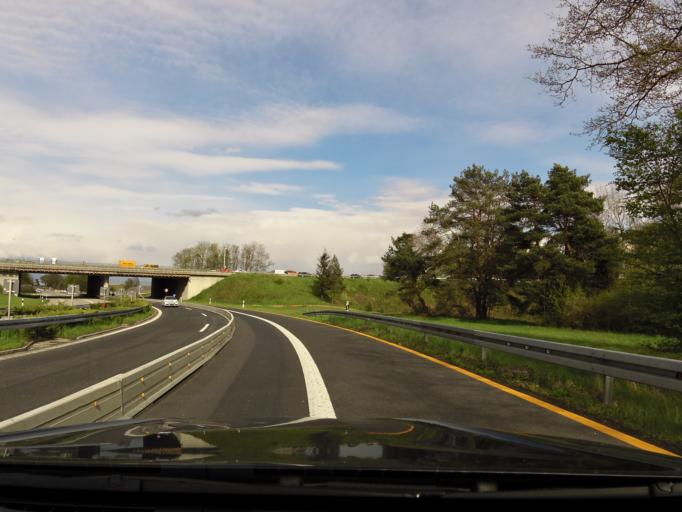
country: DE
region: Bavaria
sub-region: Upper Bavaria
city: Rohrbach
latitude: 48.5789
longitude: 11.5890
